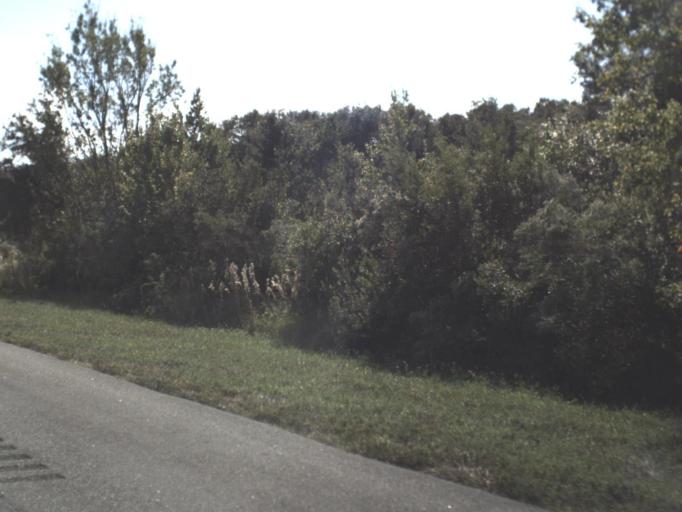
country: US
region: Florida
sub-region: Brevard County
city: June Park
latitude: 27.8415
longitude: -81.0065
